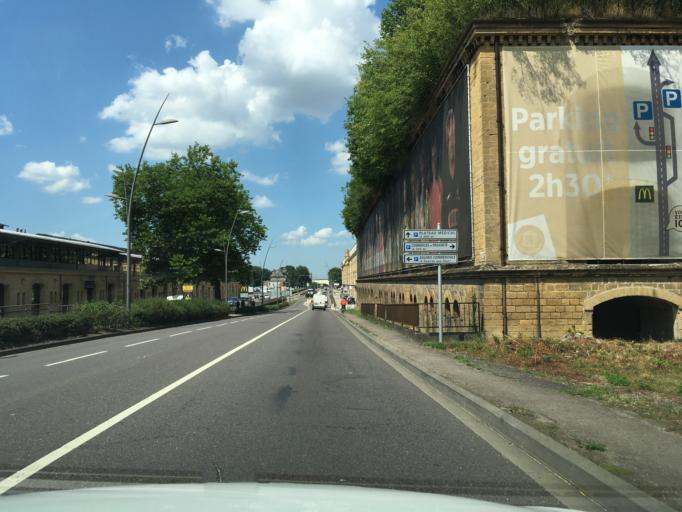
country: FR
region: Lorraine
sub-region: Departement de la Moselle
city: Metz
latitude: 49.1206
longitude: 6.1885
